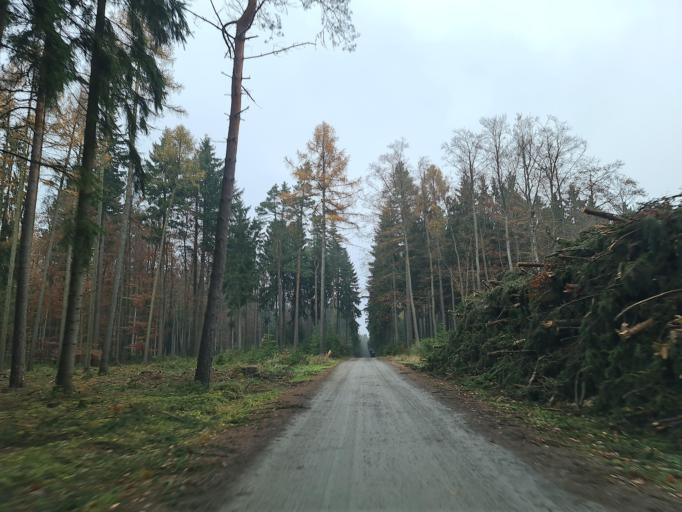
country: DE
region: Saxony
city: Mehltheuer
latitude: 50.5268
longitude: 12.0480
